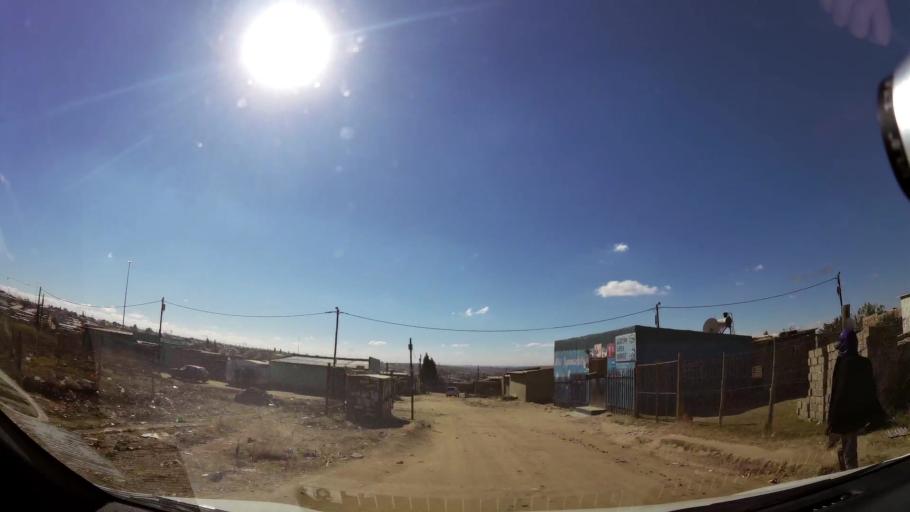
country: ZA
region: Gauteng
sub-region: City of Johannesburg Metropolitan Municipality
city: Diepsloot
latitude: -25.9199
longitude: 28.0874
